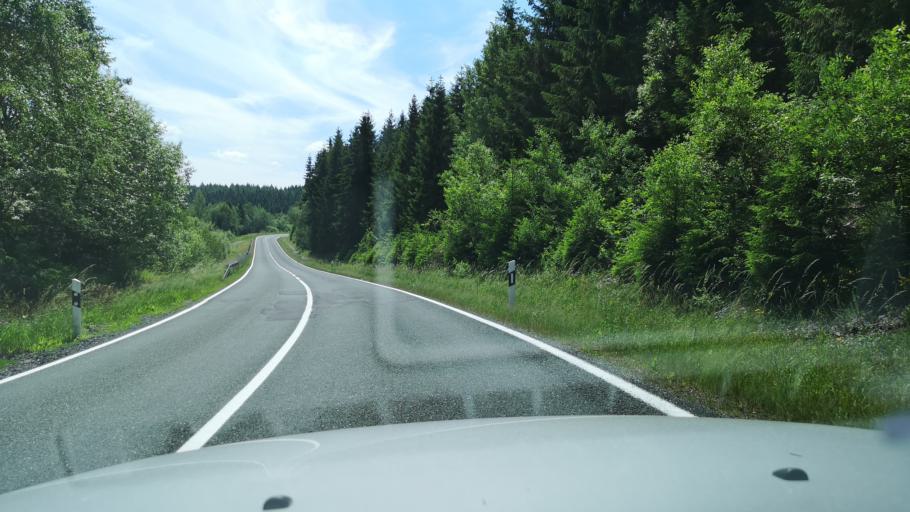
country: DE
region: Thuringia
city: Grafenthal
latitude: 50.4882
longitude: 11.2974
